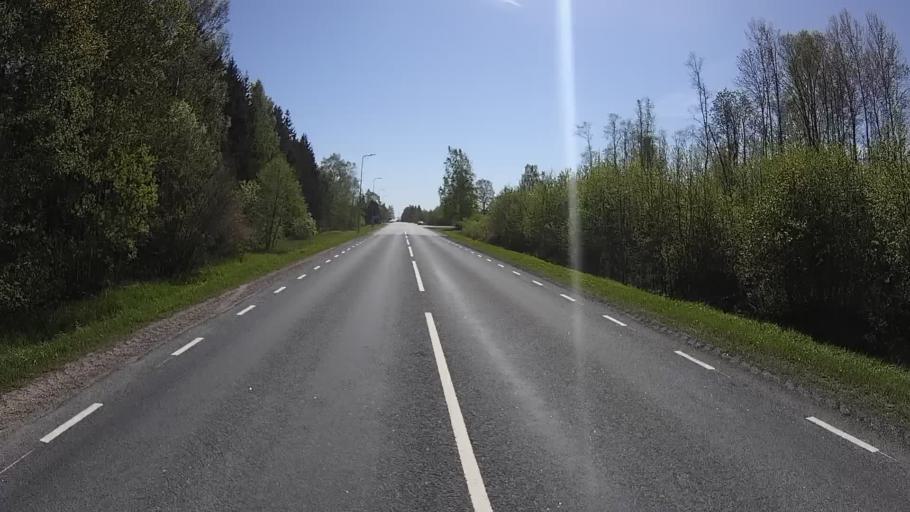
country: EE
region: Laeaene
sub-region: Lihula vald
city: Lihula
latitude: 58.5466
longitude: 23.9962
